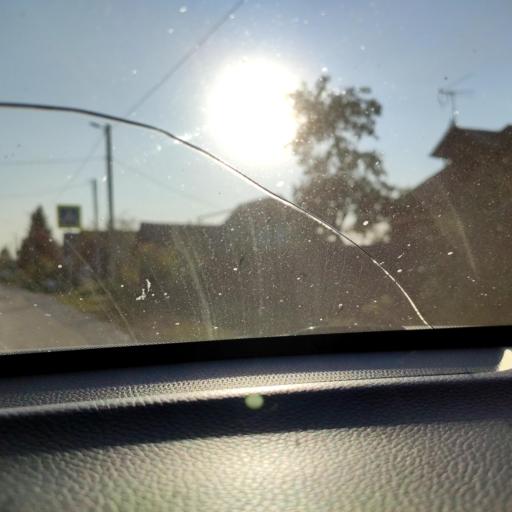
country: RU
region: Tatarstan
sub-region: Gorod Kazan'
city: Kazan
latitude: 55.7280
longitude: 49.1491
